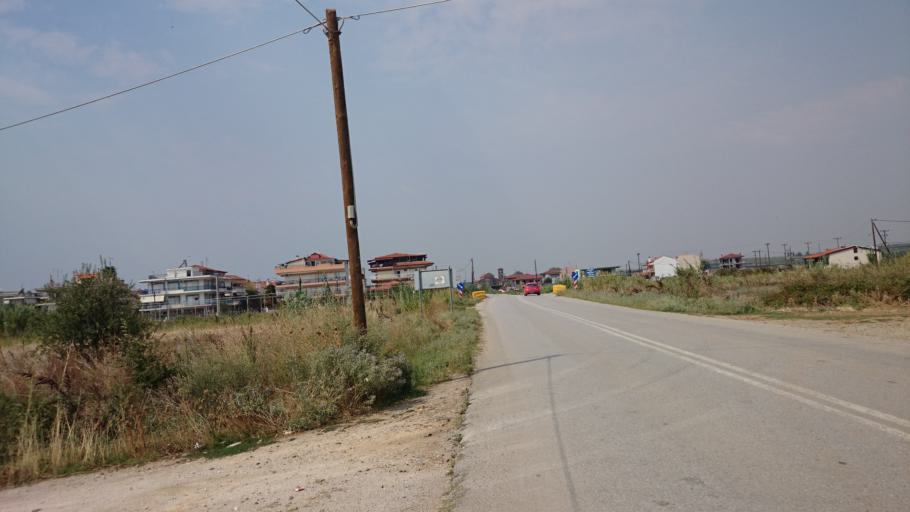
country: GR
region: Central Macedonia
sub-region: Nomos Chalkidikis
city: Nea Moudhania
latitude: 40.2505
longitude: 23.2560
